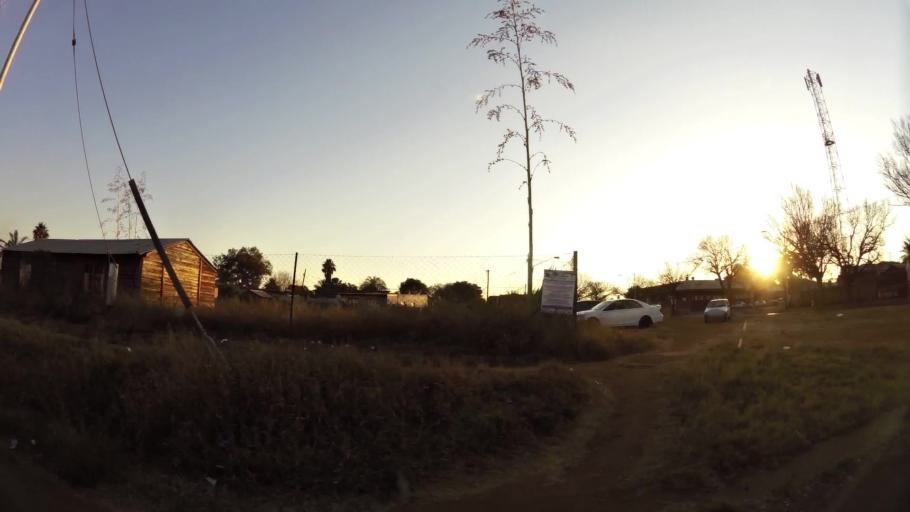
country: ZA
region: Gauteng
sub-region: City of Tshwane Metropolitan Municipality
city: Pretoria
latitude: -25.7430
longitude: 28.1221
